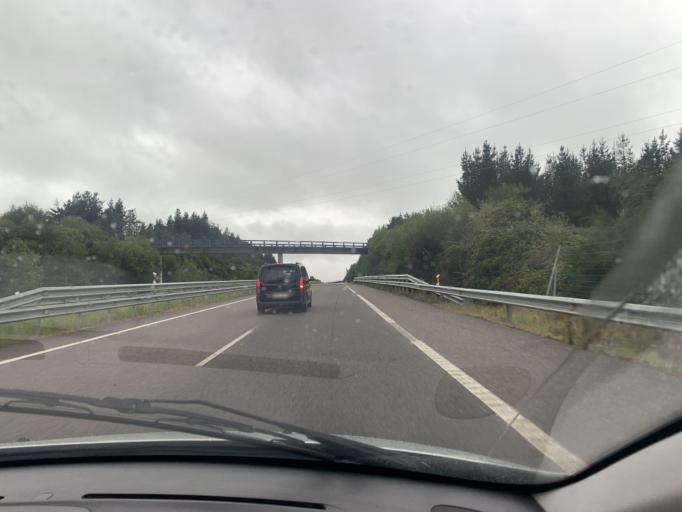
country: ES
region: Galicia
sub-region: Provincia de Lugo
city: Abadin
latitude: 43.3468
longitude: -7.5108
